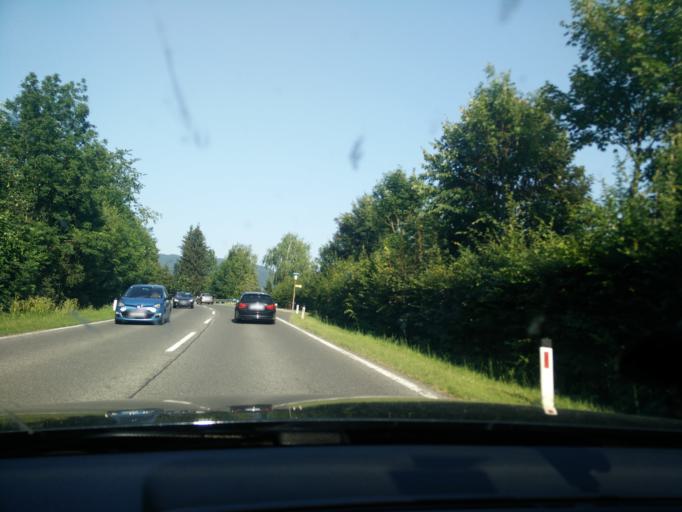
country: AT
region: Carinthia
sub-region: Politischer Bezirk Villach Land
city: Wernberg
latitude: 46.6632
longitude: 13.9204
